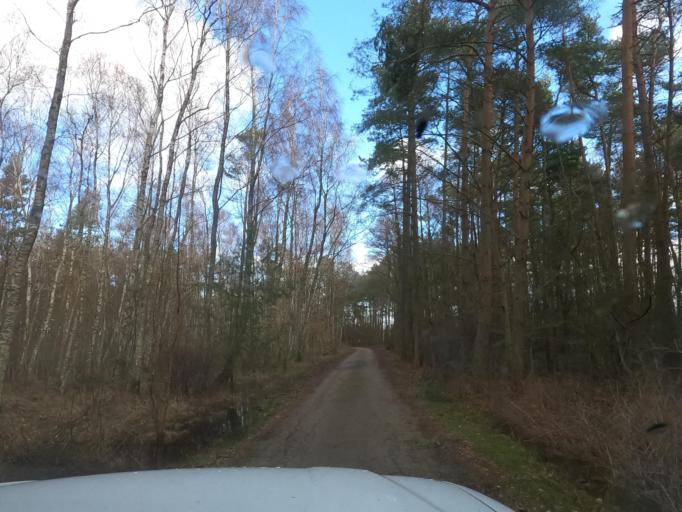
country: PL
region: West Pomeranian Voivodeship
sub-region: Powiat koszalinski
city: Sianow
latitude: 54.3487
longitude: 16.2643
